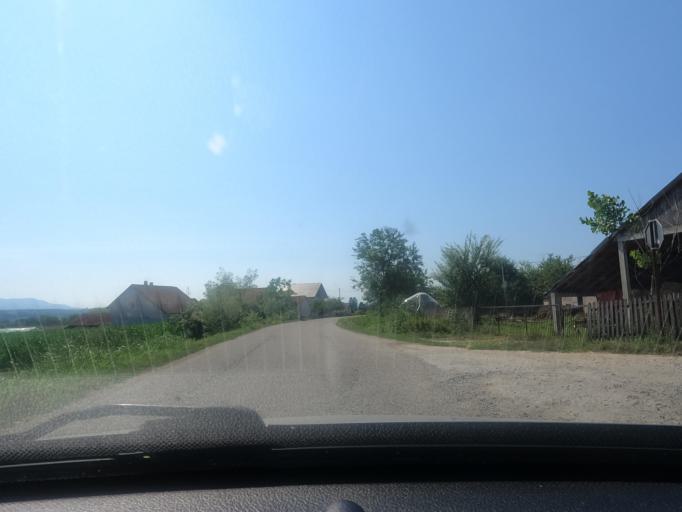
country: RS
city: Jadranska Lesnica
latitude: 44.5447
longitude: 19.3613
